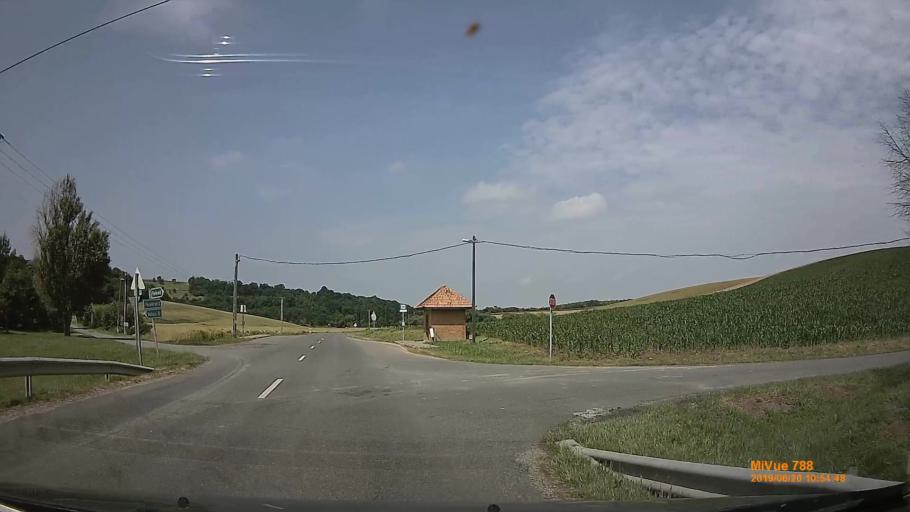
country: HU
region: Baranya
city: Mecseknadasd
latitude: 46.1534
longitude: 18.5602
